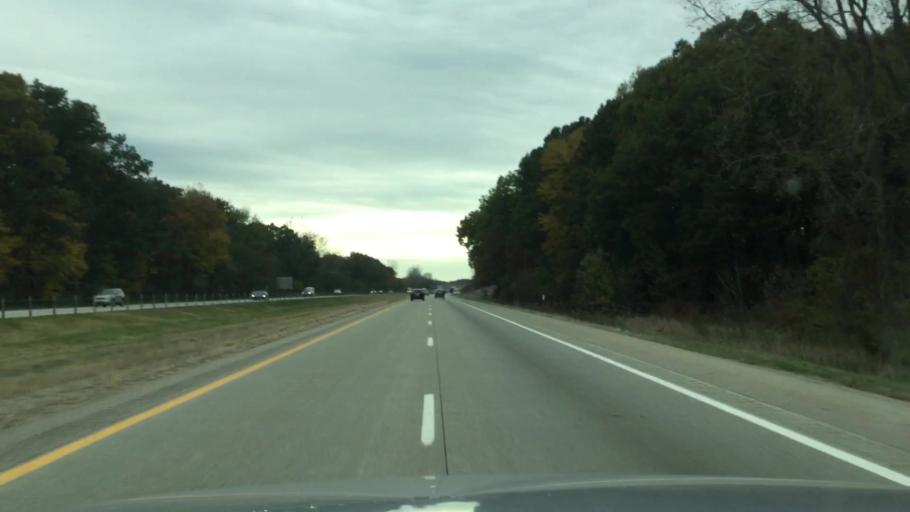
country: US
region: Michigan
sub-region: Van Buren County
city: Paw Paw
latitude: 42.2052
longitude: -85.9200
